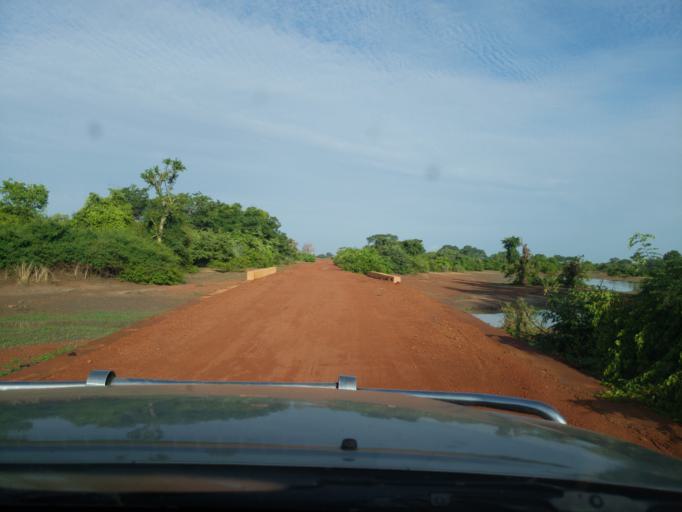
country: ML
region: Sikasso
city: Koutiala
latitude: 12.4241
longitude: -5.6659
